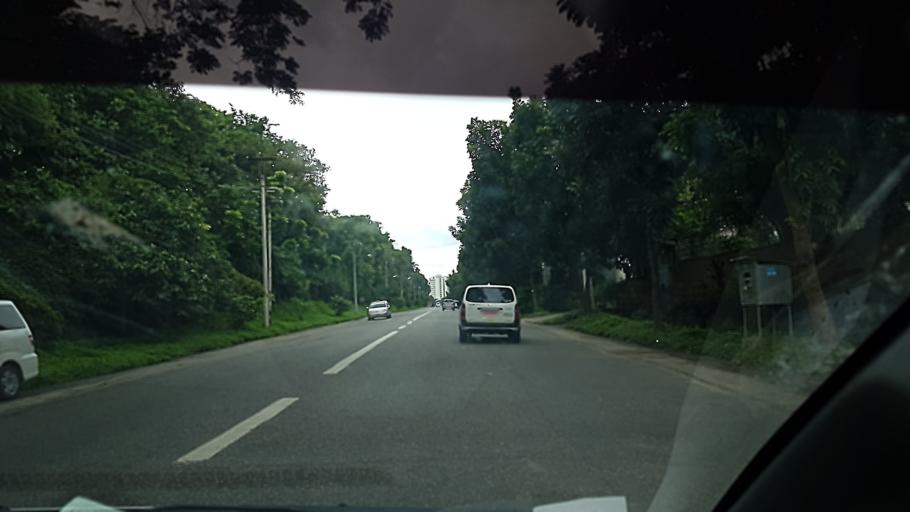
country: MM
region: Yangon
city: Yangon
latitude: 16.7949
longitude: 96.1319
